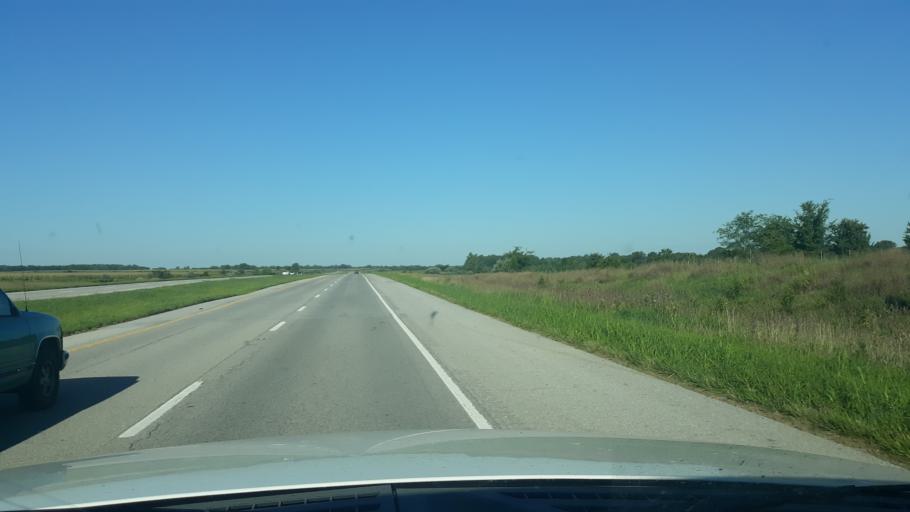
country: US
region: Illinois
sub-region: Saline County
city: Harrisburg
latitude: 37.7318
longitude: -88.5823
